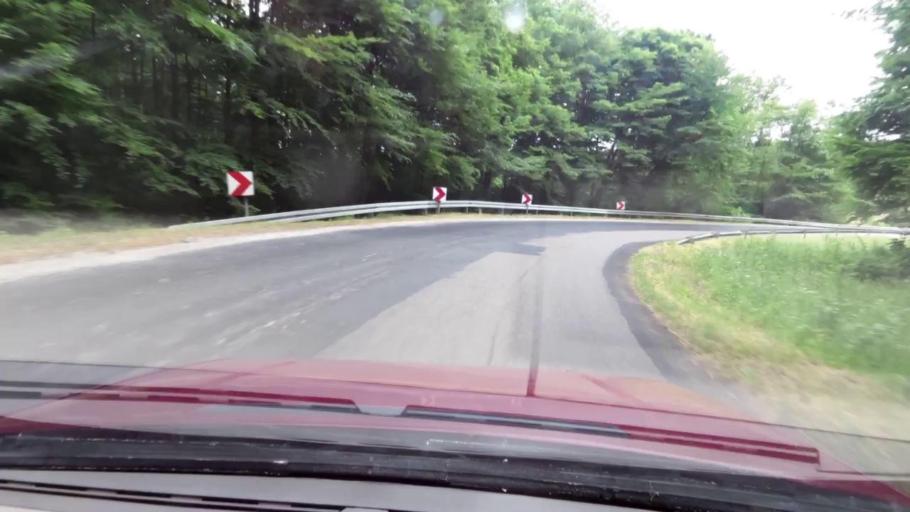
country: PL
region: Pomeranian Voivodeship
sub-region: Powiat bytowski
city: Trzebielino
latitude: 54.2677
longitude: 17.0124
